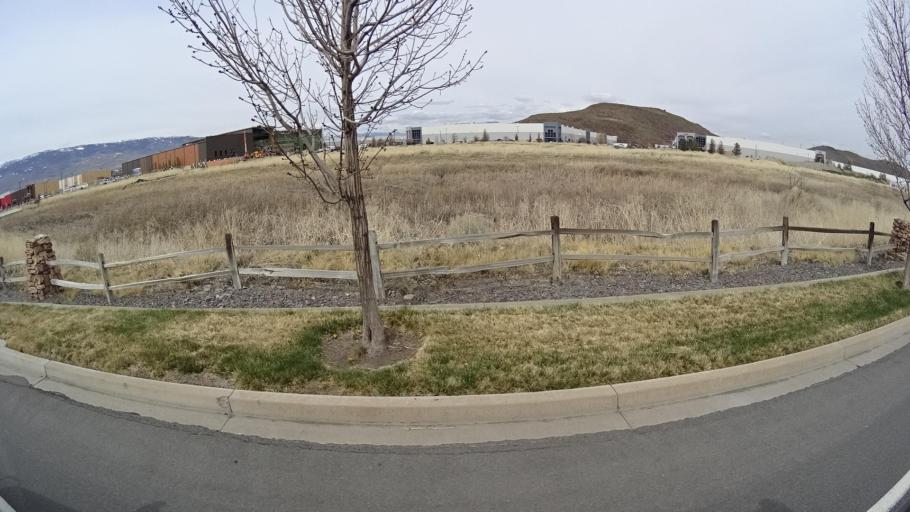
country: US
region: Nevada
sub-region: Washoe County
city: Sparks
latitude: 39.4468
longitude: -119.7424
